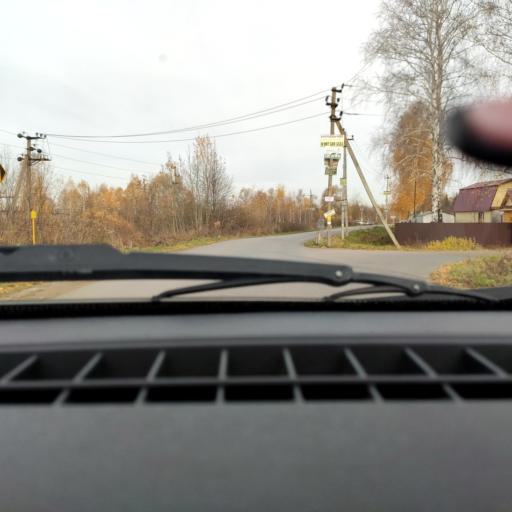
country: RU
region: Bashkortostan
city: Iglino
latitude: 54.8102
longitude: 56.1889
